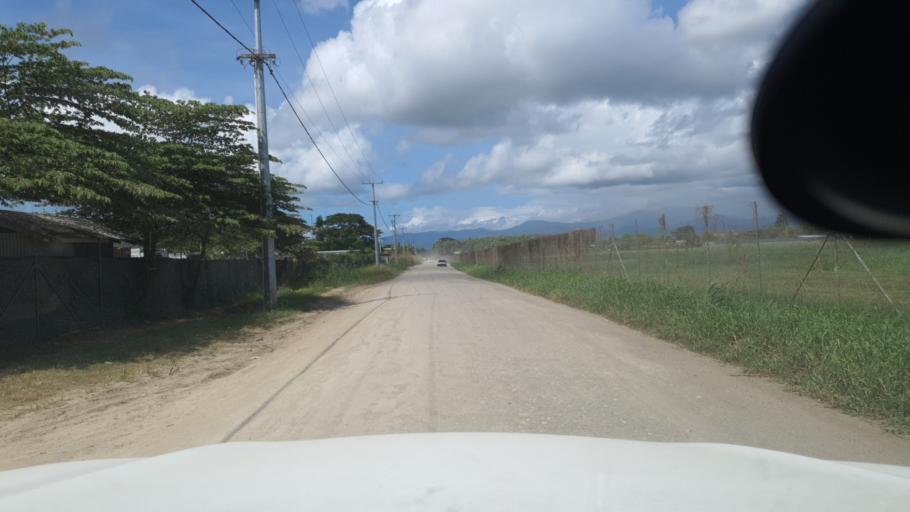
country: SB
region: Guadalcanal
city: Honiara
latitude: -9.4217
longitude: 160.0362
